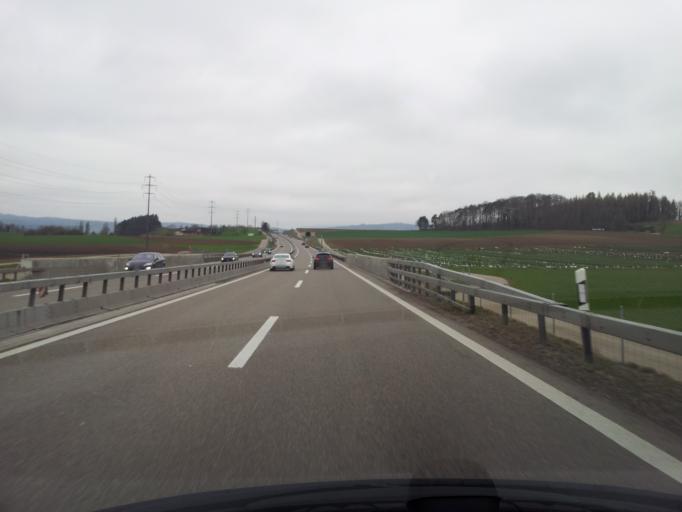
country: CH
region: Zurich
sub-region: Bezirk Andelfingen
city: Uhwiesen
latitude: 47.6545
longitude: 8.6401
